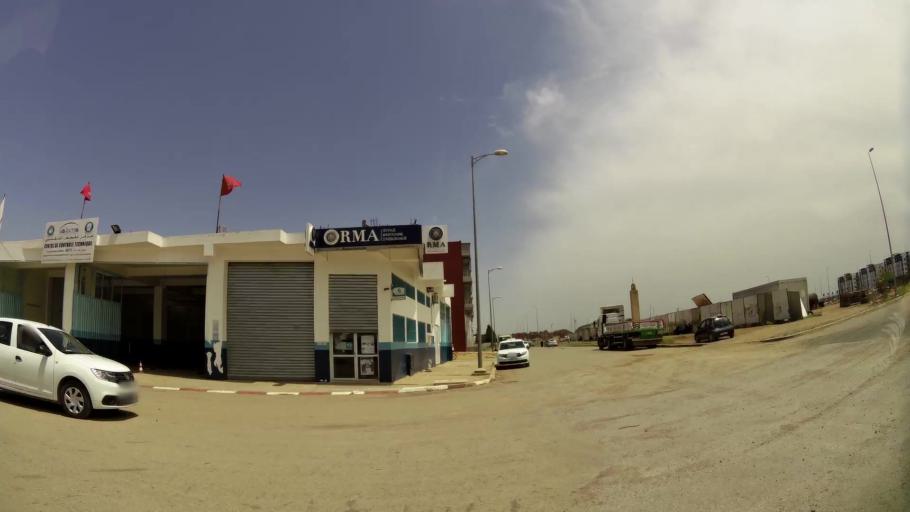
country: MA
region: Rabat-Sale-Zemmour-Zaer
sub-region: Khemisset
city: Khemisset
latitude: 33.8203
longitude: -6.0852
